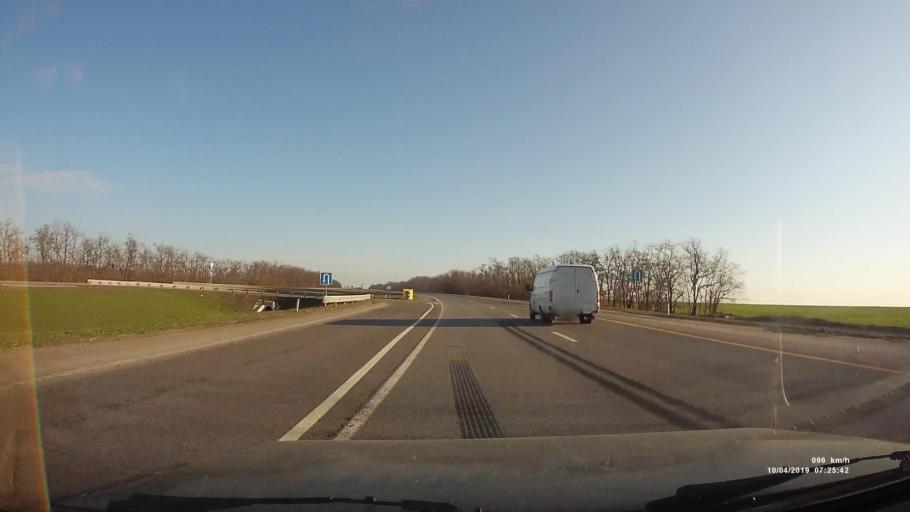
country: RU
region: Rostov
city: Gornyy
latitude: 47.8980
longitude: 40.2186
